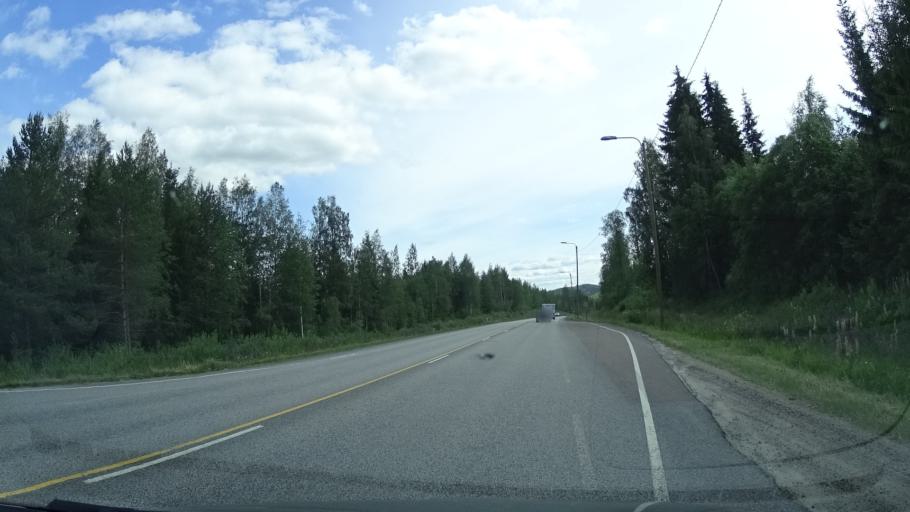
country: FI
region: Central Finland
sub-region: Jyvaeskylae
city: Jyvaeskylae
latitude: 62.2603
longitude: 25.6003
